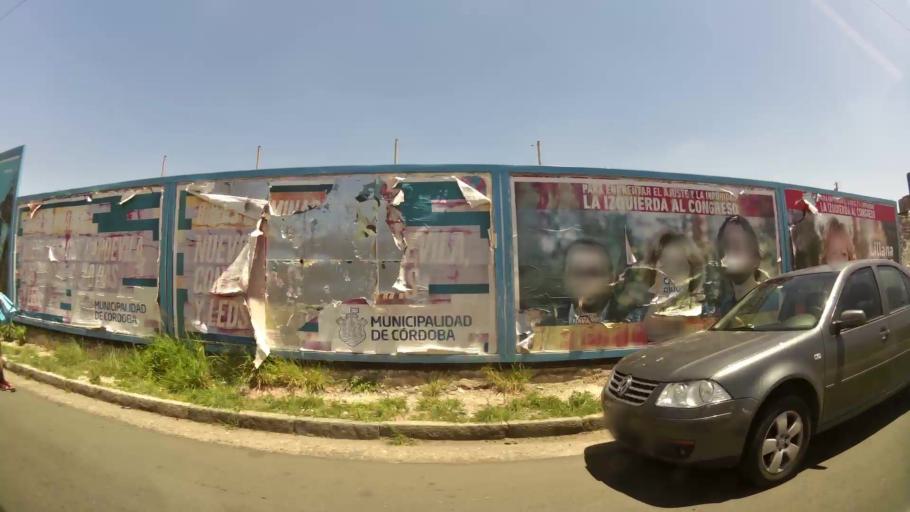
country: AR
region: Cordoba
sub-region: Departamento de Capital
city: Cordoba
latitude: -31.4007
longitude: -64.2059
